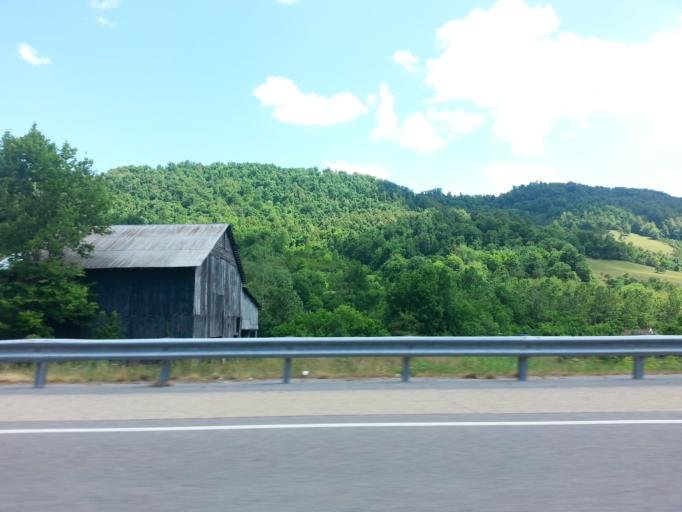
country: US
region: Virginia
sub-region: Lee County
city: Dryden
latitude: 36.7115
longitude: -82.9578
